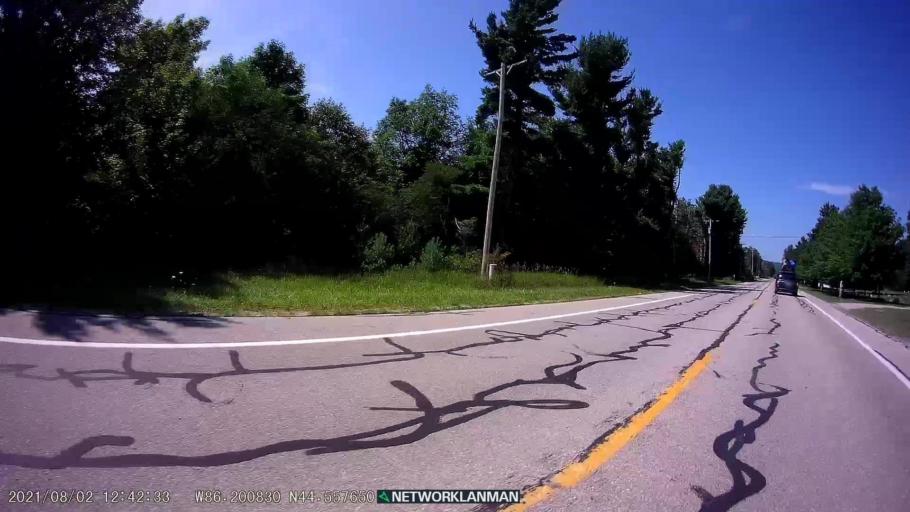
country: US
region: Michigan
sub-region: Benzie County
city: Frankfort
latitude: 44.5580
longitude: -86.2008
